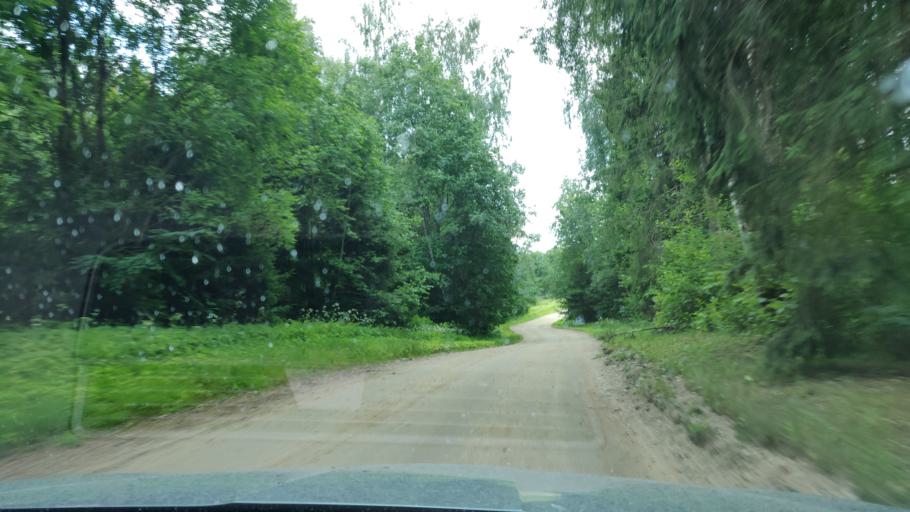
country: EE
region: Vorumaa
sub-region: Antsla vald
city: Vana-Antsla
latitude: 58.0337
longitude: 26.5520
